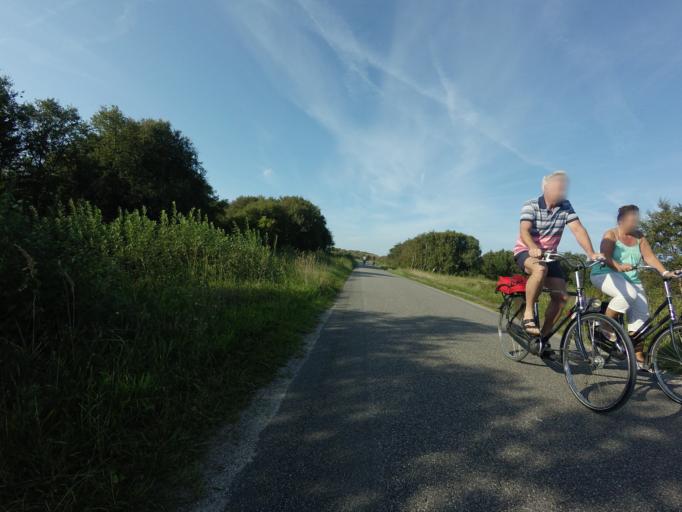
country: NL
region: Friesland
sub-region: Gemeente Schiermonnikoog
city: Schiermonnikoog
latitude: 53.4947
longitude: 6.1854
